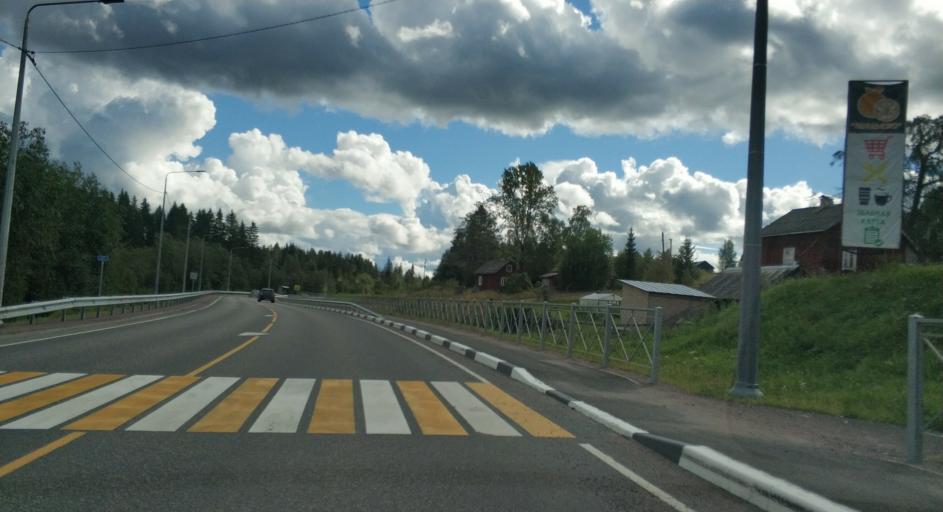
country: RU
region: Republic of Karelia
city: Ruskeala
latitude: 61.9320
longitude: 30.5939
